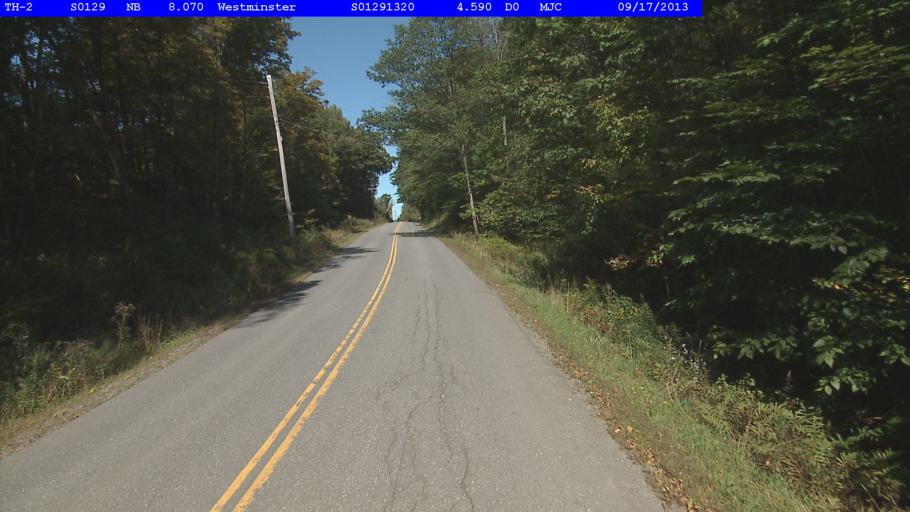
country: US
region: Vermont
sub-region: Windham County
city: Bellows Falls
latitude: 43.0811
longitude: -72.5359
